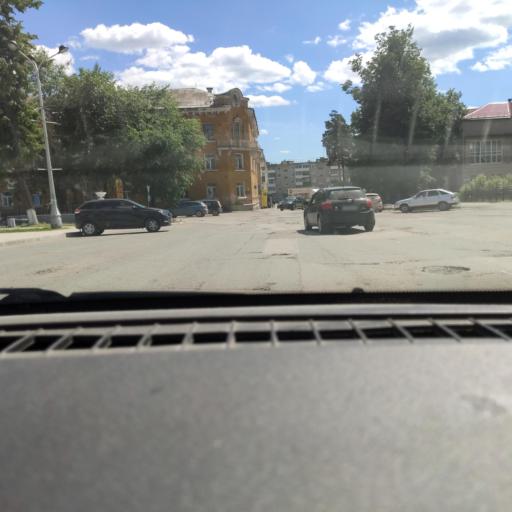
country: RU
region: Perm
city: Krasnokamsk
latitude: 58.0783
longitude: 55.7361
